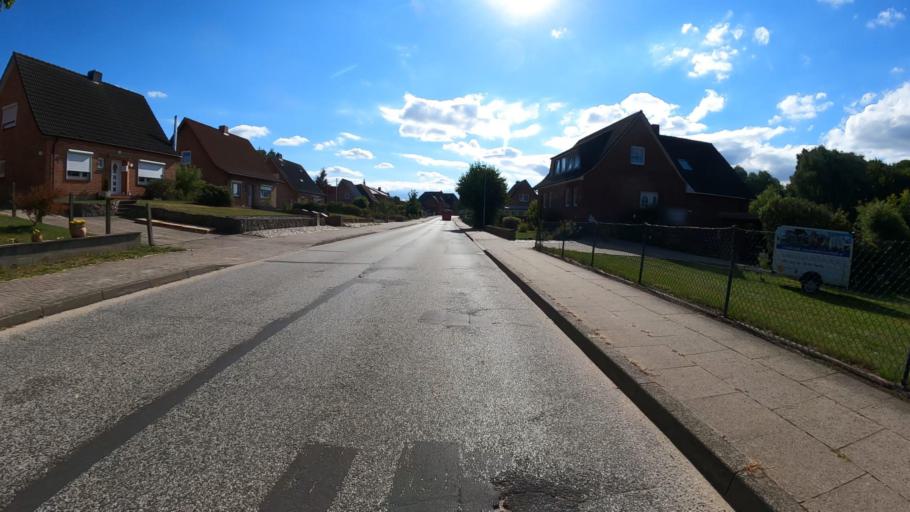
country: DE
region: Schleswig-Holstein
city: Lasbek
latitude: 53.7060
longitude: 10.3835
